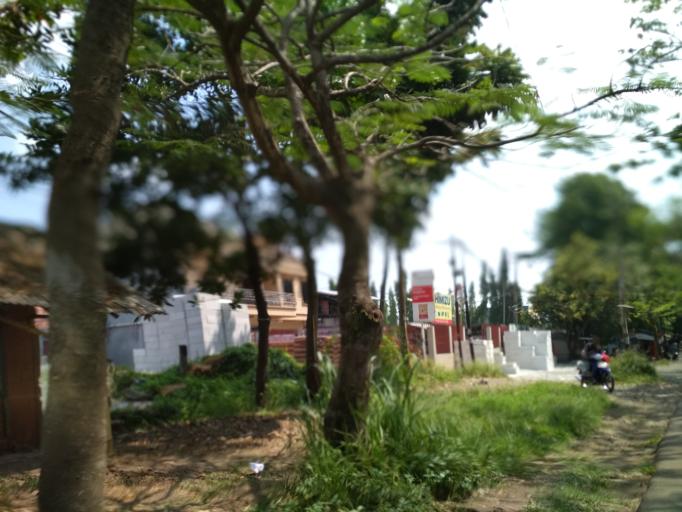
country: ID
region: West Java
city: Bogor
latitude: -6.5677
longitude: 106.7535
